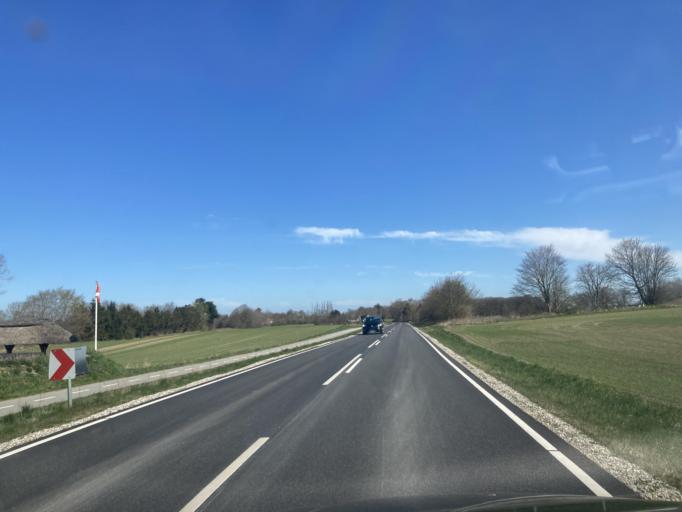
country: DK
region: Capital Region
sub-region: Gribskov Kommune
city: Graested
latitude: 56.0984
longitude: 12.2219
